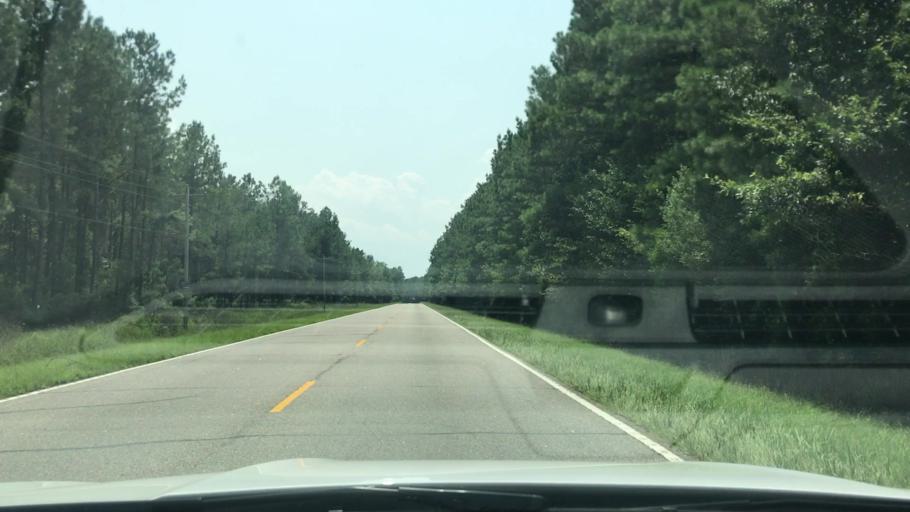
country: US
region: South Carolina
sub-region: Georgetown County
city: Georgetown
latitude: 33.5003
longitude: -79.2588
